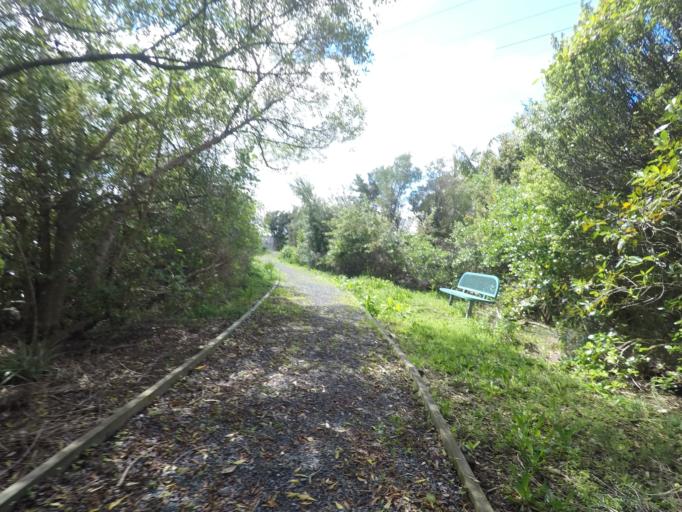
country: NZ
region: Auckland
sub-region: Auckland
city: Rosebank
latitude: -36.8783
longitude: 174.6650
